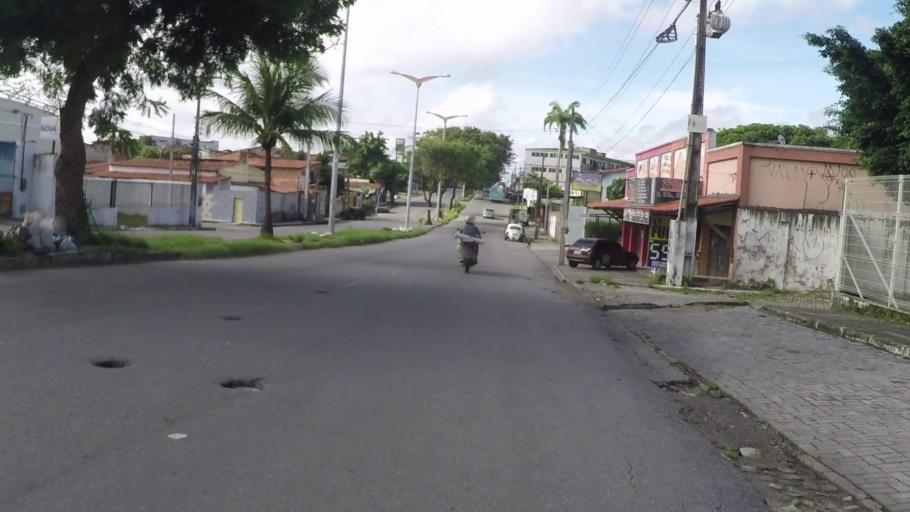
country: BR
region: Ceara
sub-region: Fortaleza
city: Fortaleza
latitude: -3.7149
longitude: -38.5887
